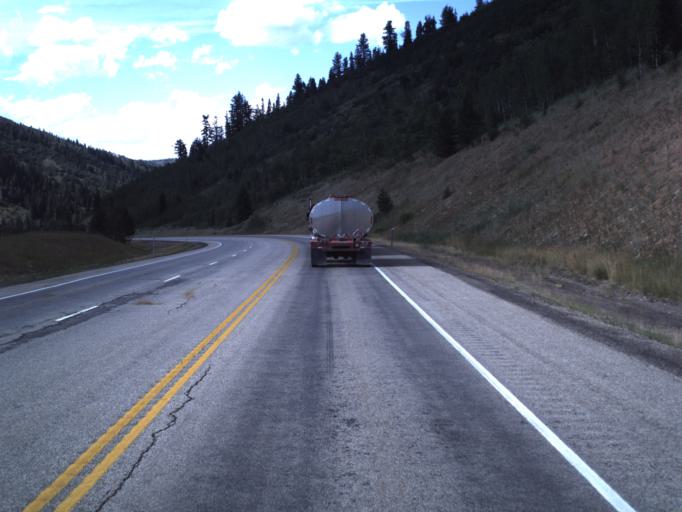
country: US
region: Utah
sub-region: Wasatch County
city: Heber
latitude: 40.3196
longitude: -111.2586
